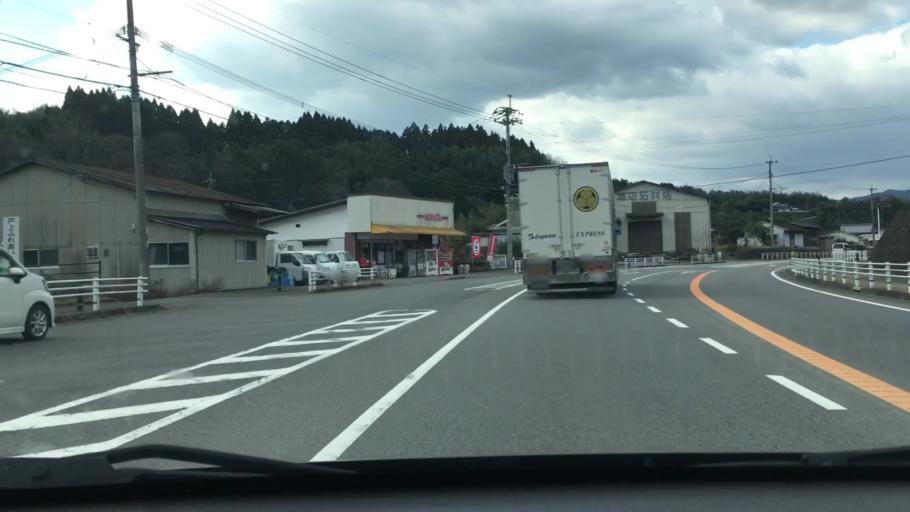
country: JP
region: Oita
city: Usuki
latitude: 33.0651
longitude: 131.6598
